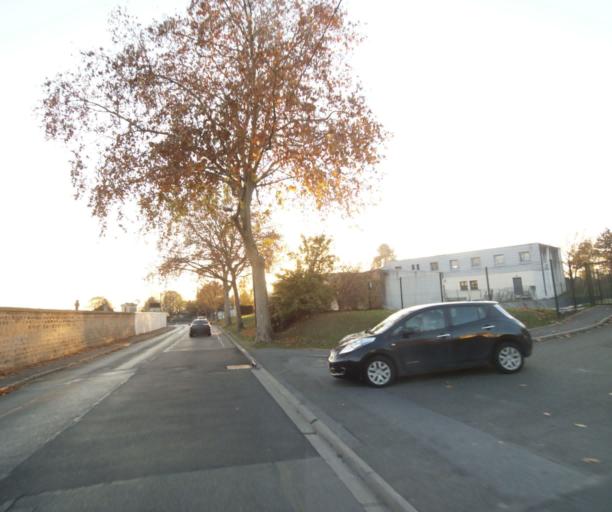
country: FR
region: Ile-de-France
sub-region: Departement du Val-d'Oise
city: Gonesse
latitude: 48.9914
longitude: 2.4531
